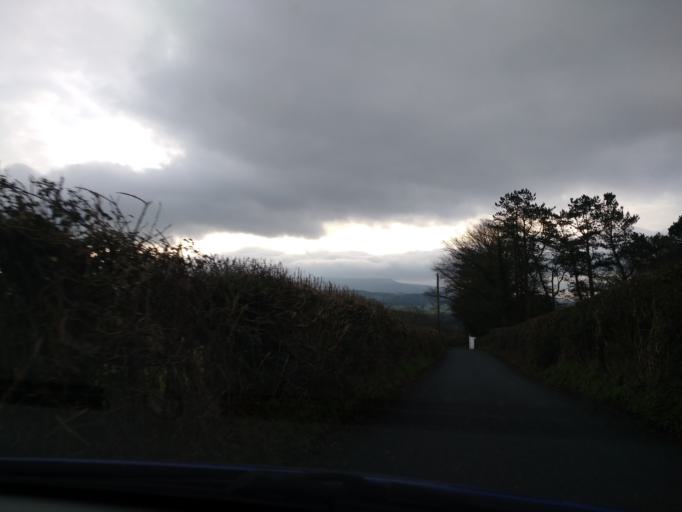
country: GB
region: England
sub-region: Lancashire
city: Caton
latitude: 54.0866
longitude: -2.7420
